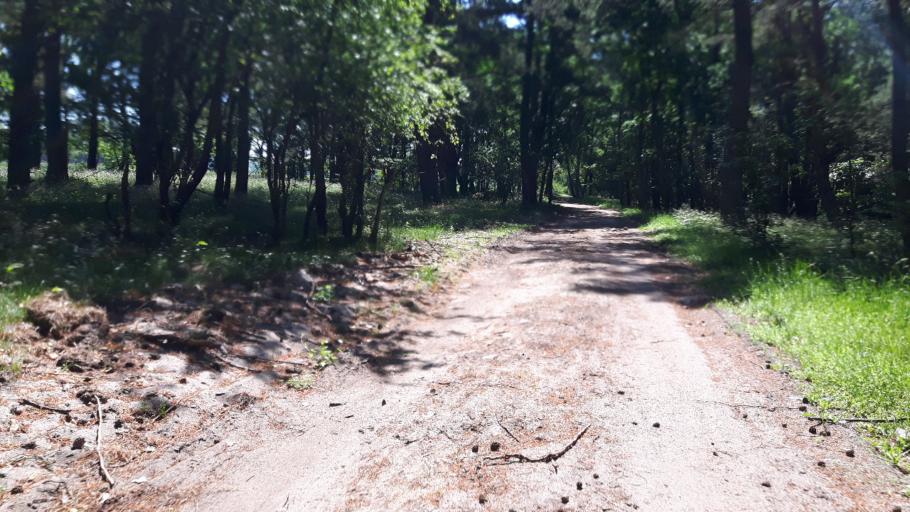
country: PL
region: Pomeranian Voivodeship
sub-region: Powiat slupski
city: Smoldzino
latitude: 54.6763
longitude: 17.1556
